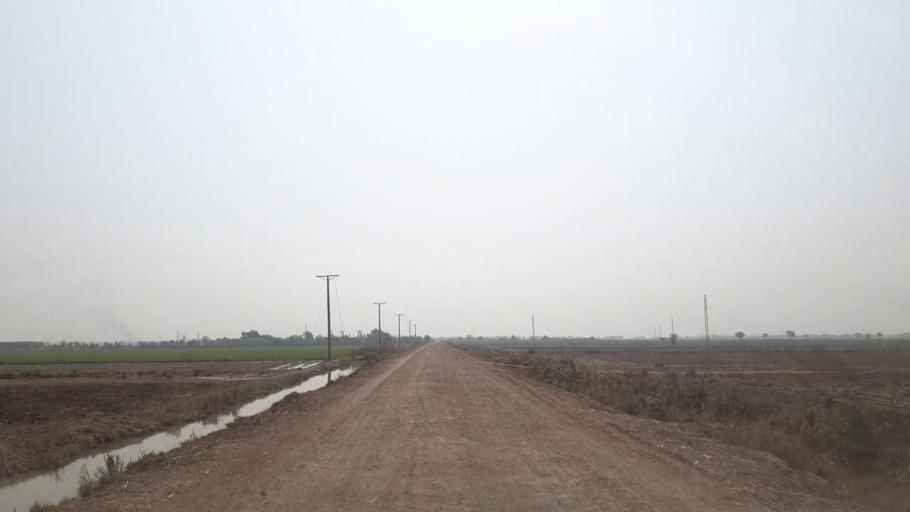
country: PK
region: Sindh
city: Mirpur Khas
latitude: 25.5466
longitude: 69.0594
